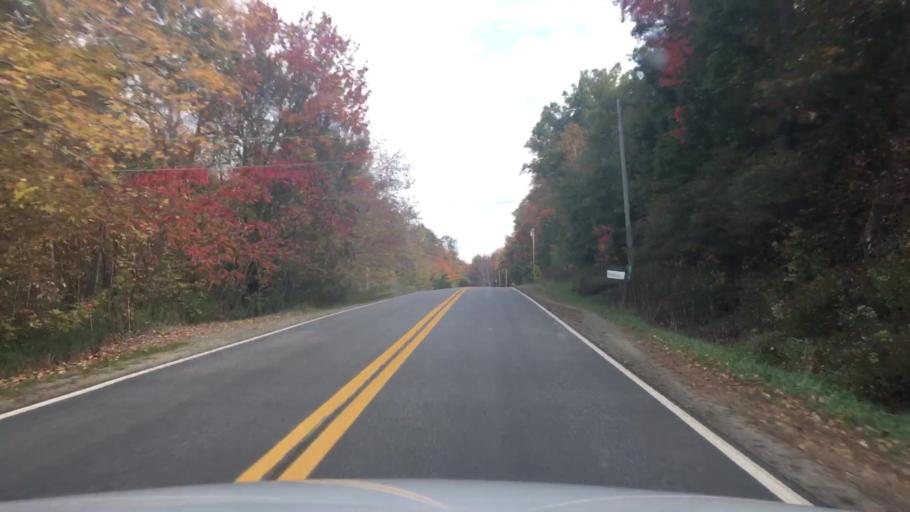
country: US
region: Maine
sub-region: Waldo County
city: Searsmont
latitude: 44.3361
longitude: -69.1391
